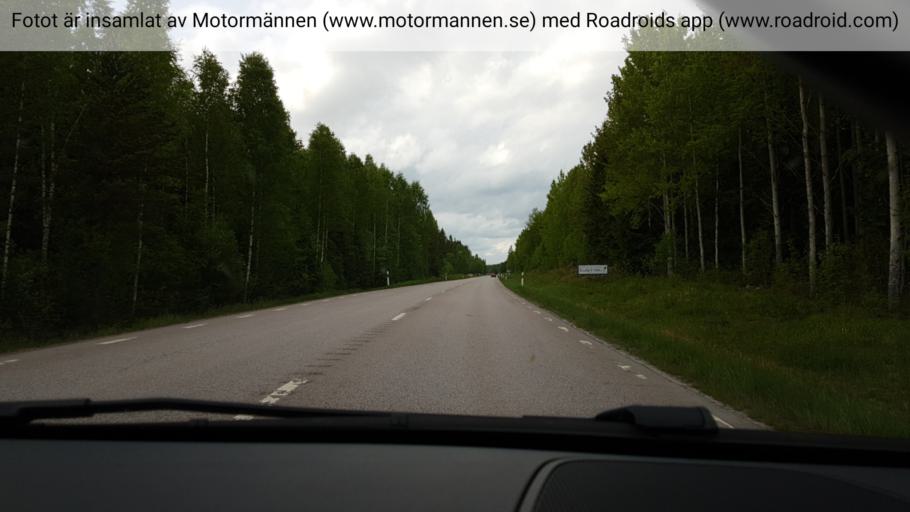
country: SE
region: Uppsala
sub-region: Tierps Kommun
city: Orbyhus
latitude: 60.2648
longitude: 17.6122
